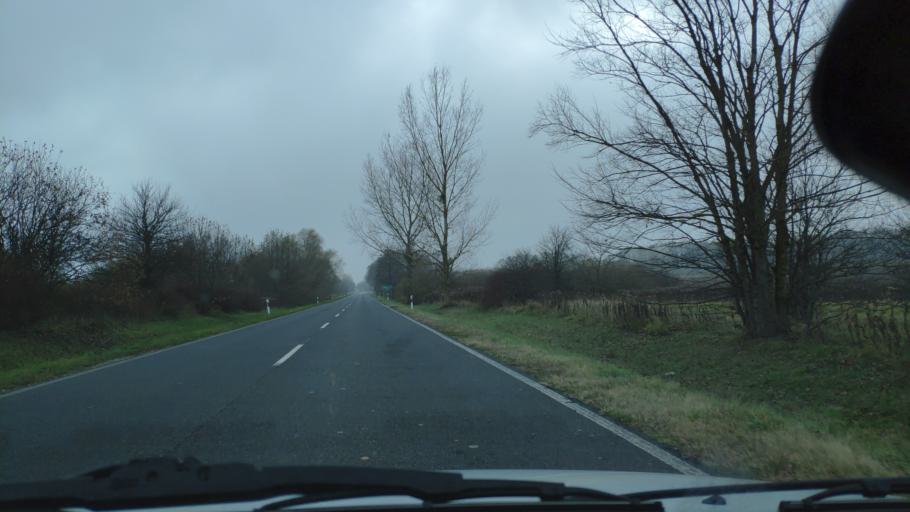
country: HU
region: Somogy
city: Balatonbereny
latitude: 46.6077
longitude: 17.2715
